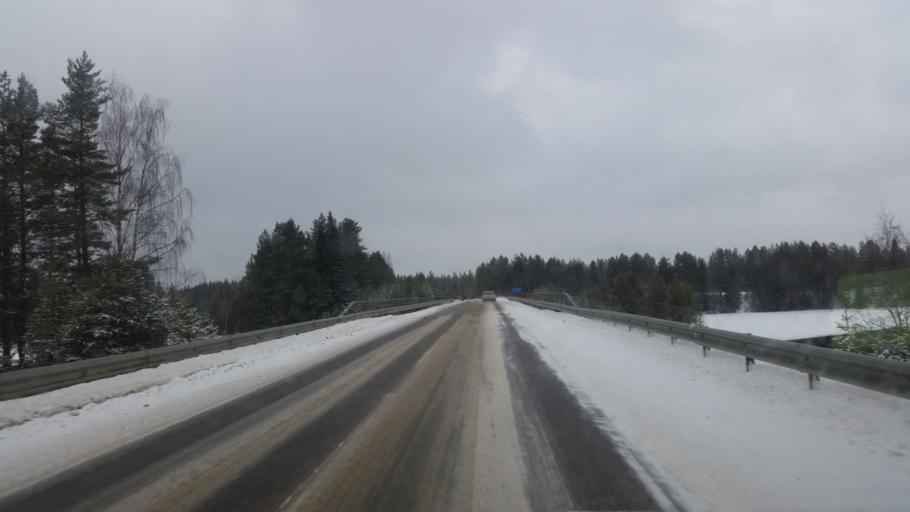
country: SE
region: Jaemtland
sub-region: Harjedalens Kommun
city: Sveg
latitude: 62.1215
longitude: 15.0372
